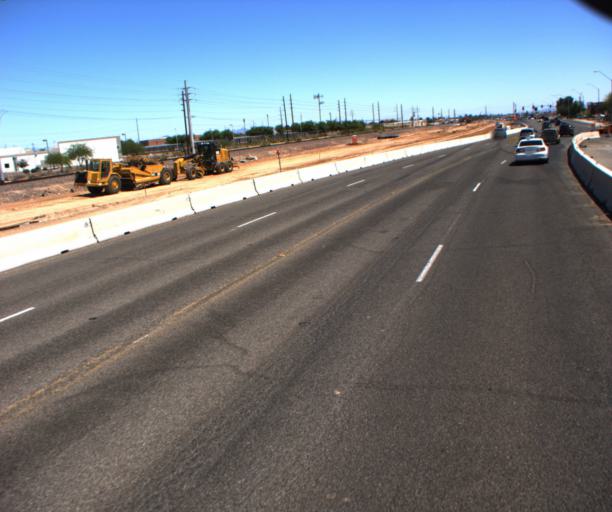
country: US
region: Arizona
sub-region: Maricopa County
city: Surprise
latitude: 33.6379
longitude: -112.3495
